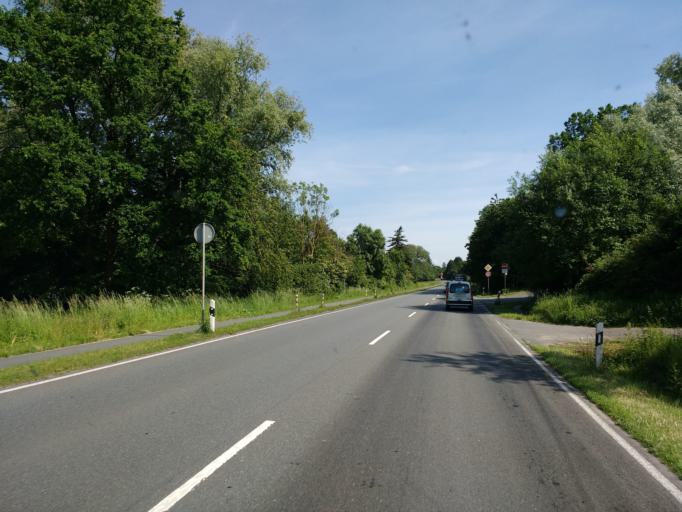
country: DE
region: North Rhine-Westphalia
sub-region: Regierungsbezirk Detmold
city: Bad Salzuflen
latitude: 52.0844
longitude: 8.7141
